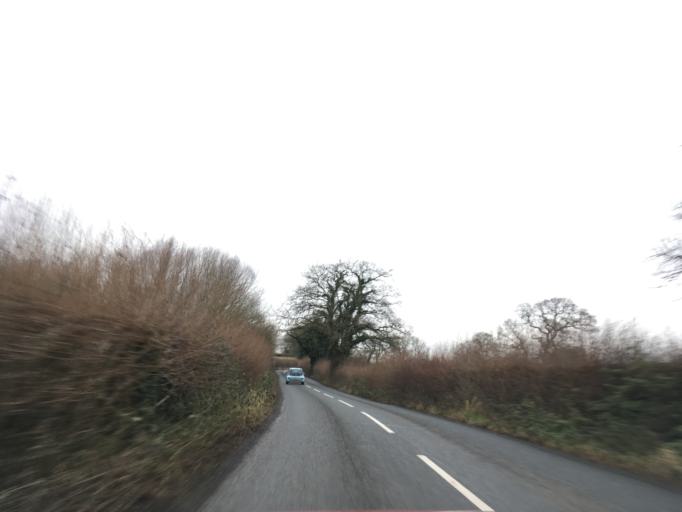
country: GB
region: England
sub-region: Gloucestershire
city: Wotton-under-Edge
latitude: 51.6081
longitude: -2.3413
